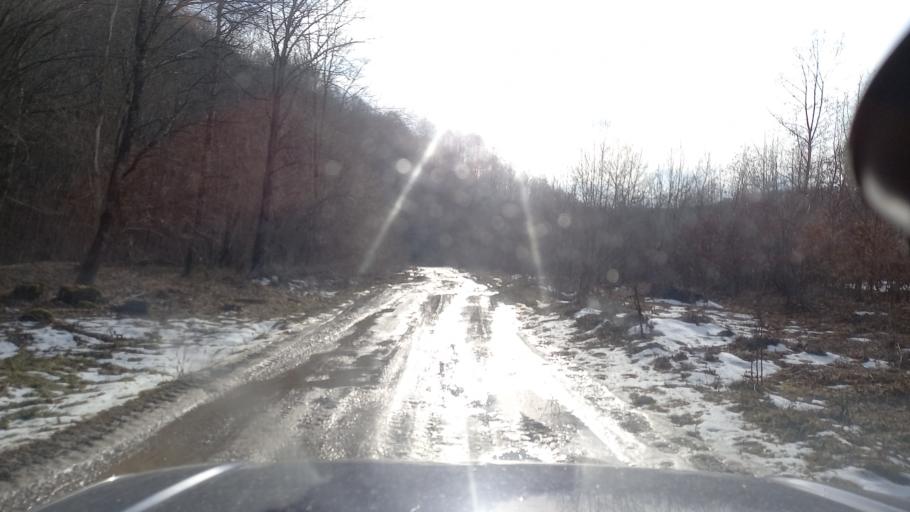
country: RU
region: Adygeya
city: Kamennomostskiy
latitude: 44.1426
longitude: 40.3050
